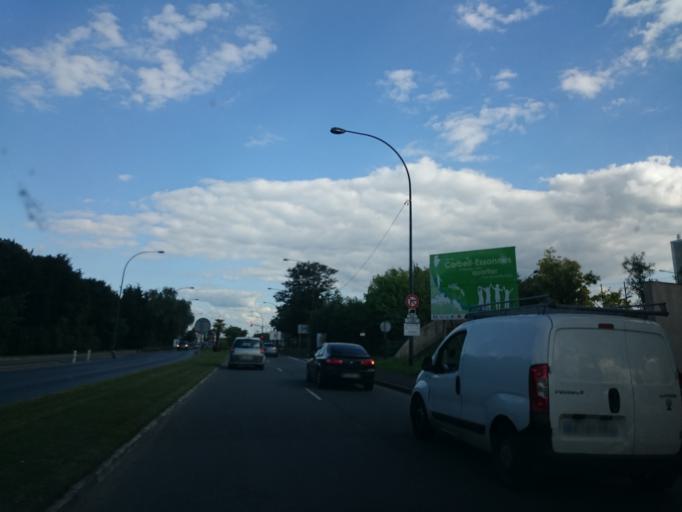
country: FR
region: Ile-de-France
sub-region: Departement de l'Essonne
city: Evry
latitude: 48.6153
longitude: 2.4570
